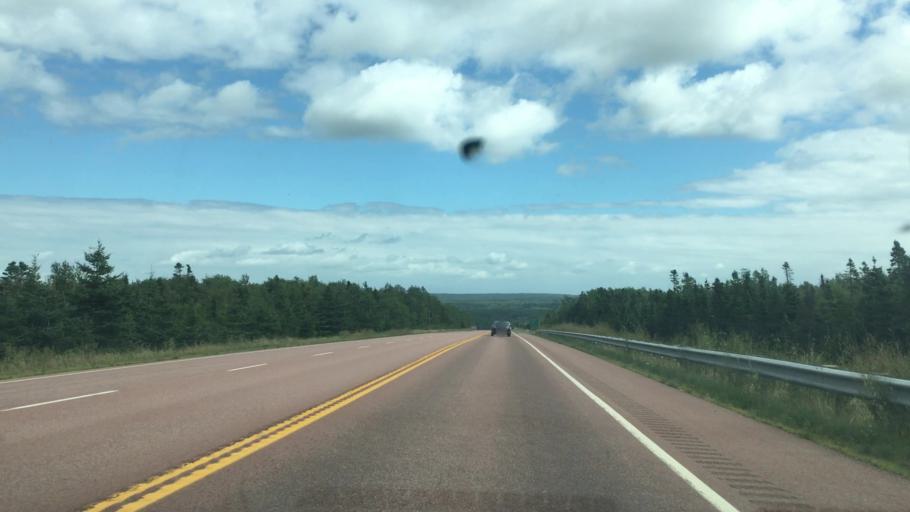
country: CA
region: Nova Scotia
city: Port Hawkesbury
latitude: 45.6107
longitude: -61.6444
